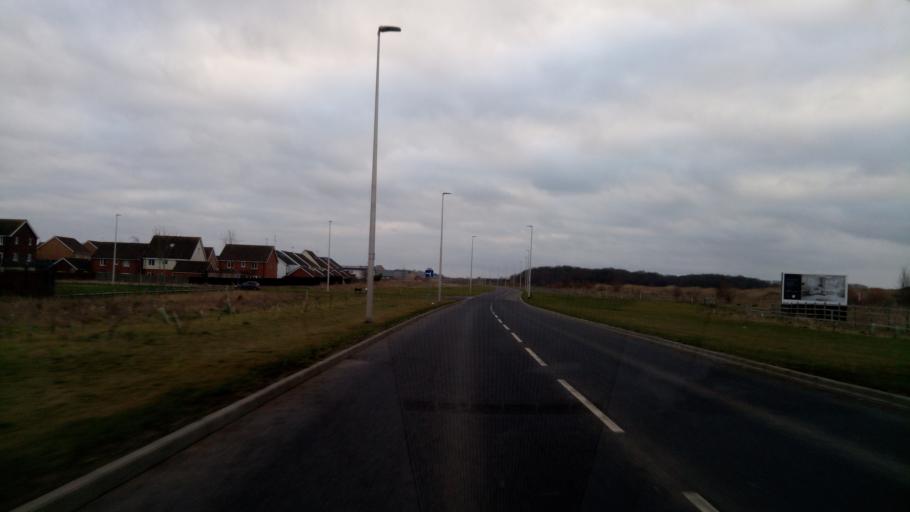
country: GB
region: England
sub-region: Cambridgeshire
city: Yaxley
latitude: 52.5349
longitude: -0.2833
